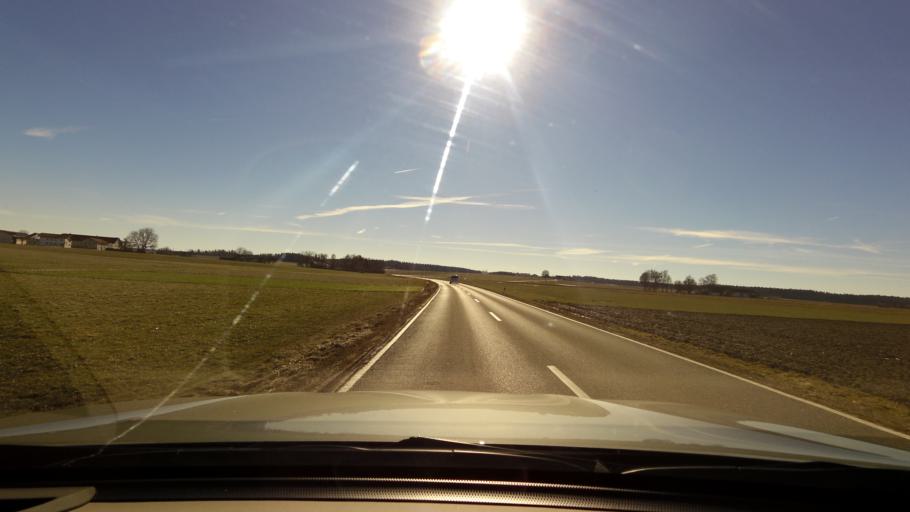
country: DE
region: Bavaria
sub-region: Upper Bavaria
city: Taufkirchen
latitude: 48.1732
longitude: 12.4603
